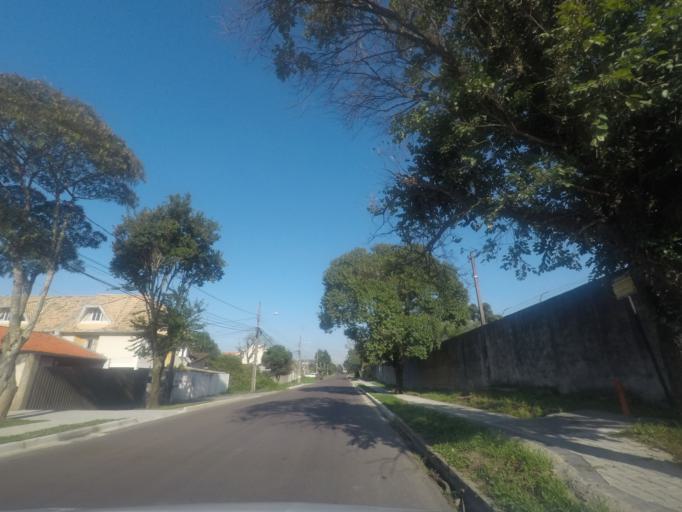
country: BR
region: Parana
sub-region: Pinhais
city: Pinhais
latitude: -25.4709
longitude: -49.2130
